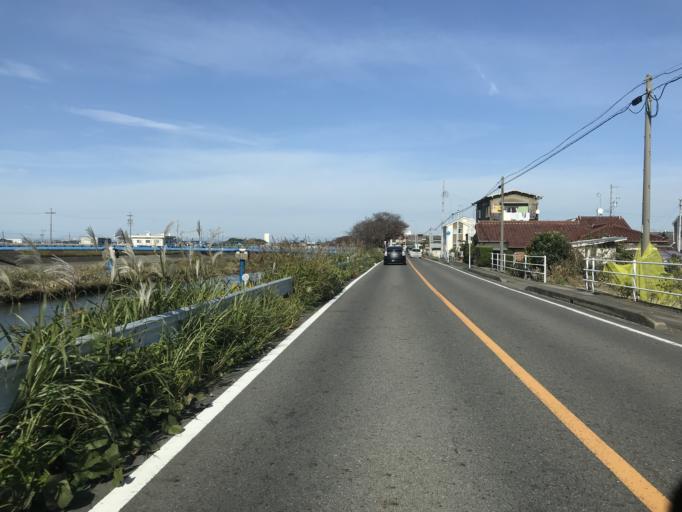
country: JP
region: Aichi
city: Iwakura
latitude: 35.2233
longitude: 136.8459
